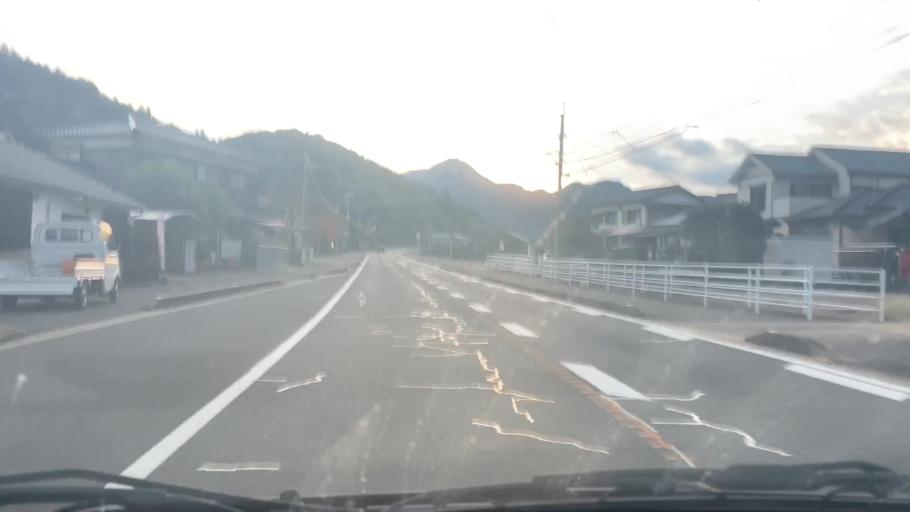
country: JP
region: Saga Prefecture
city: Kashima
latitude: 33.0884
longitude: 130.0815
